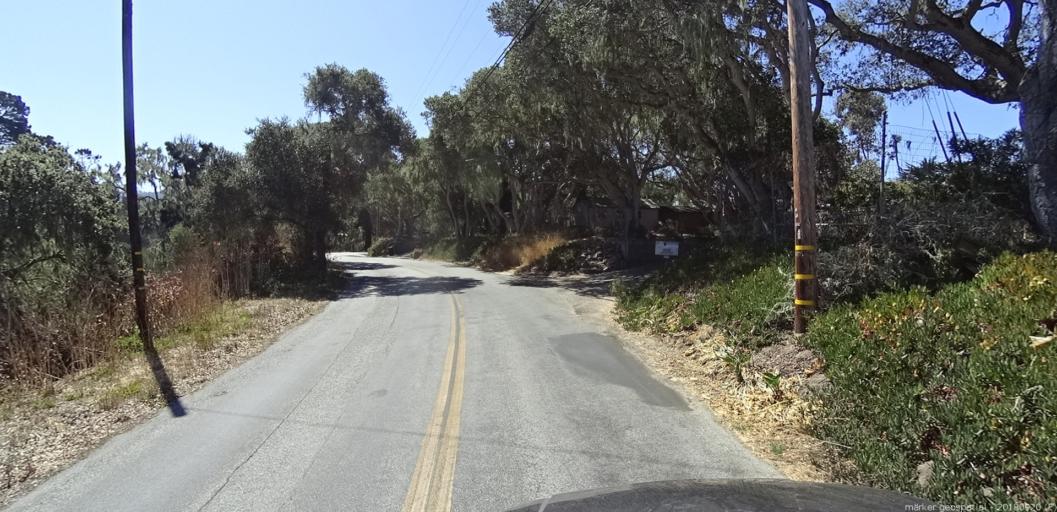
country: US
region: California
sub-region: Monterey County
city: Monterey
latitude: 36.5904
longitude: -121.8709
